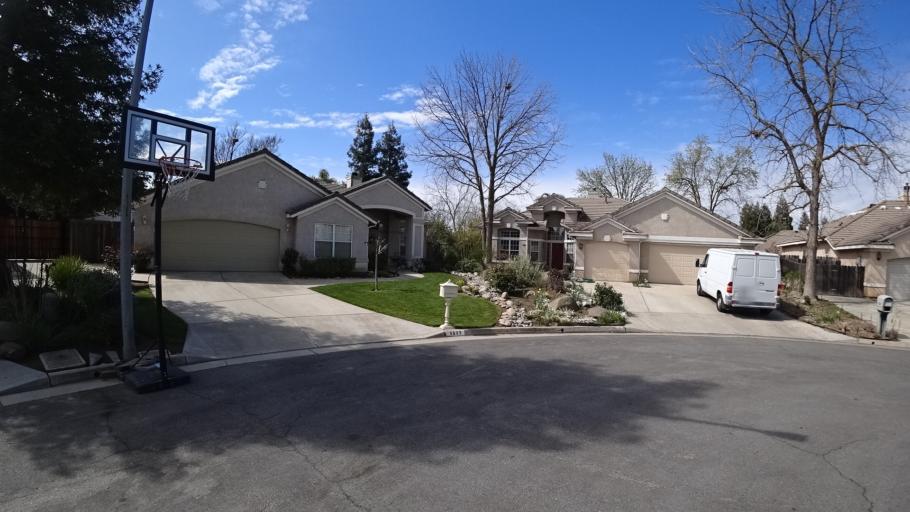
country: US
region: California
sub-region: Fresno County
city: Biola
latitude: 36.8504
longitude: -119.8907
